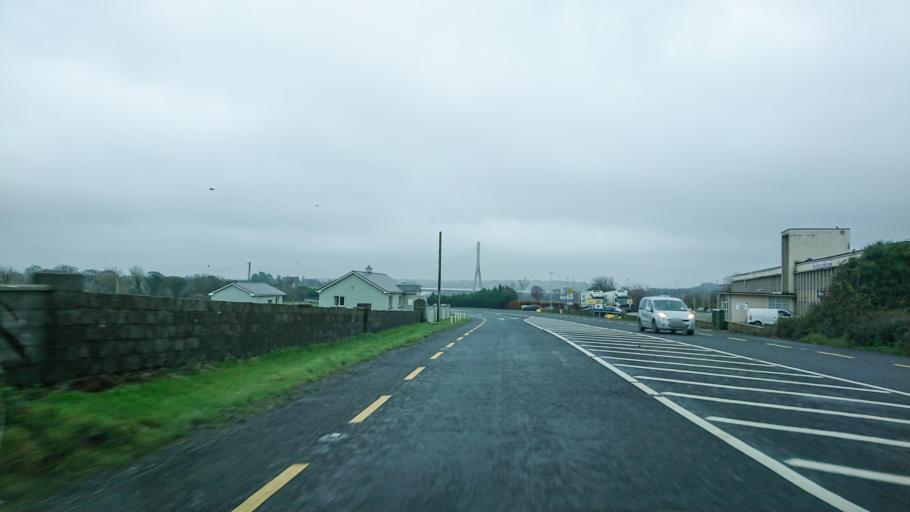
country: IE
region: Munster
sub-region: Waterford
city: Waterford
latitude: 52.2806
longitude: -7.1687
